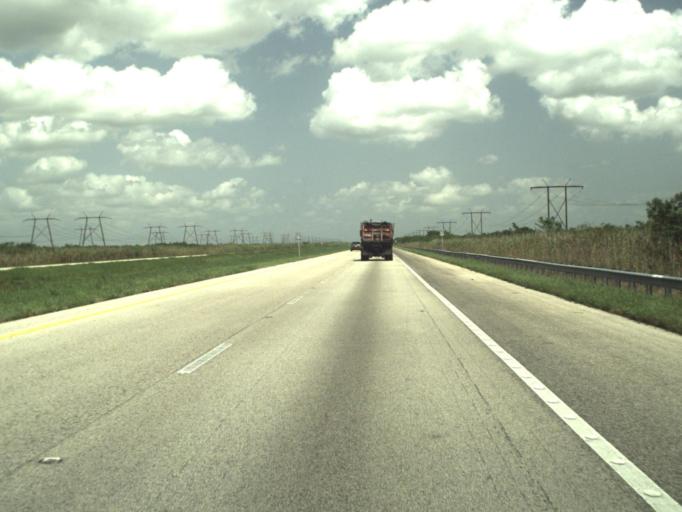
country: US
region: Florida
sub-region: Broward County
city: Weston
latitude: 26.2593
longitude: -80.4793
